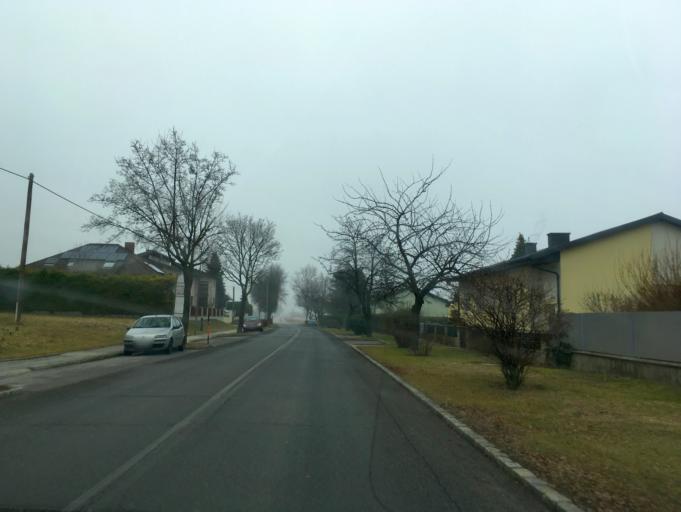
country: AT
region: Lower Austria
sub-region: Politischer Bezirk Bruck an der Leitha
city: Trautmannsdorf an der Leitha
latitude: 48.0525
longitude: 16.6480
